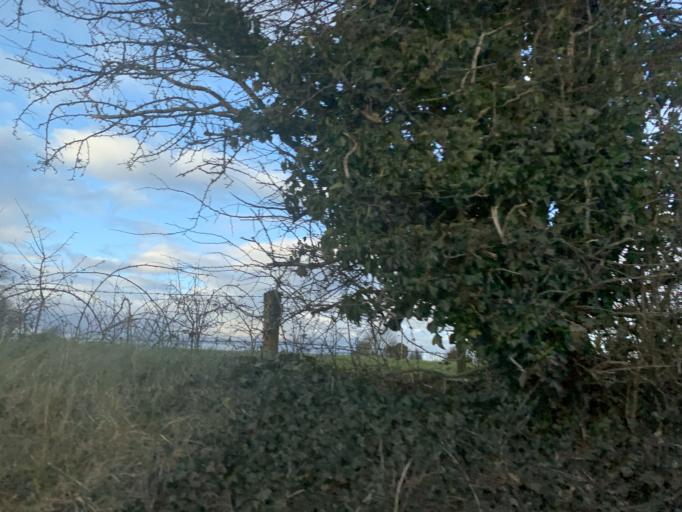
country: IE
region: Connaught
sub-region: Maigh Eo
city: Ballyhaunis
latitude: 53.8611
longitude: -8.7467
